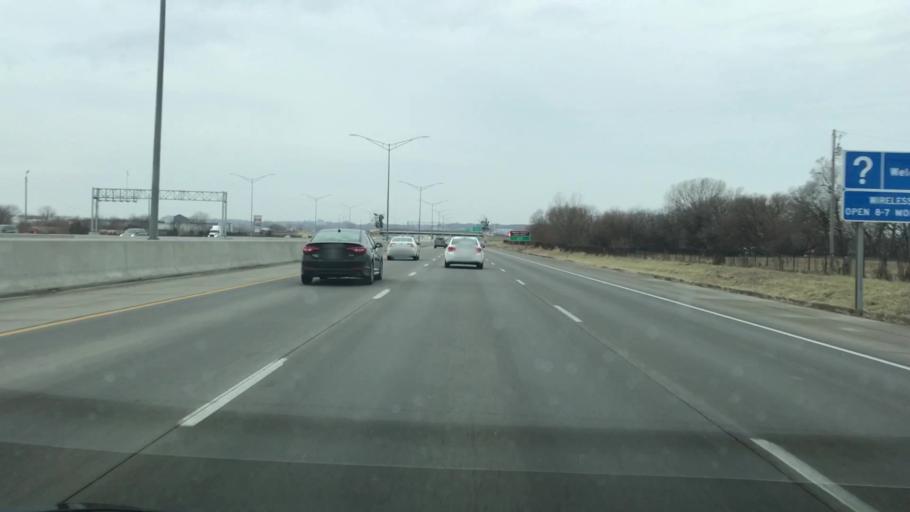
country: US
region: Iowa
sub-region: Pottawattamie County
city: Council Bluffs
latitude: 41.2326
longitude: -95.8684
